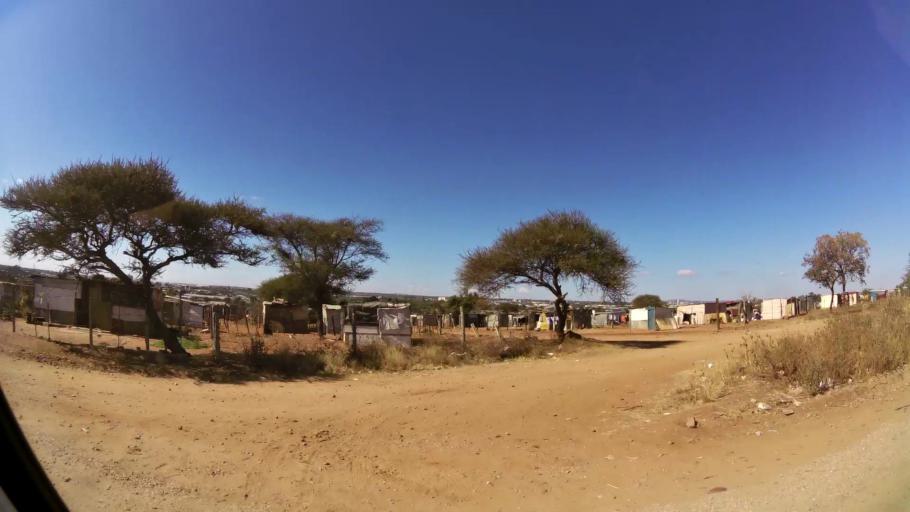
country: ZA
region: Limpopo
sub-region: Capricorn District Municipality
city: Polokwane
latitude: -23.8782
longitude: 29.4262
